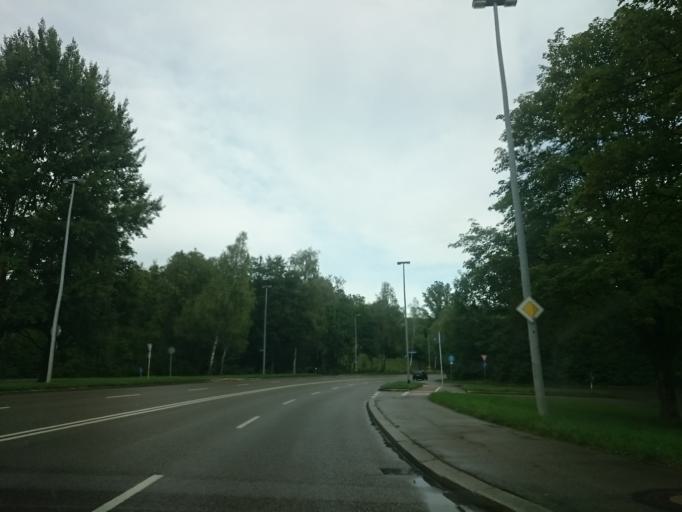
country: DE
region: Bavaria
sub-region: Swabia
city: Kempten (Allgaeu)
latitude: 47.7385
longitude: 10.3174
